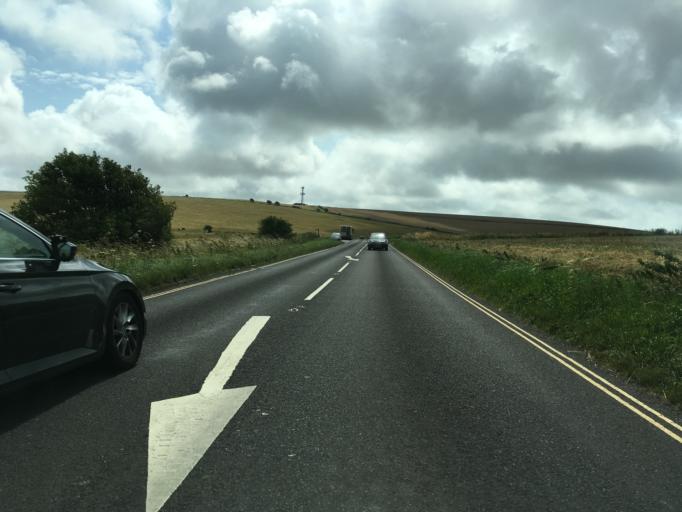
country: GB
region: England
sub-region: Brighton and Hove
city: Rottingdean
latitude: 50.8518
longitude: -0.0735
